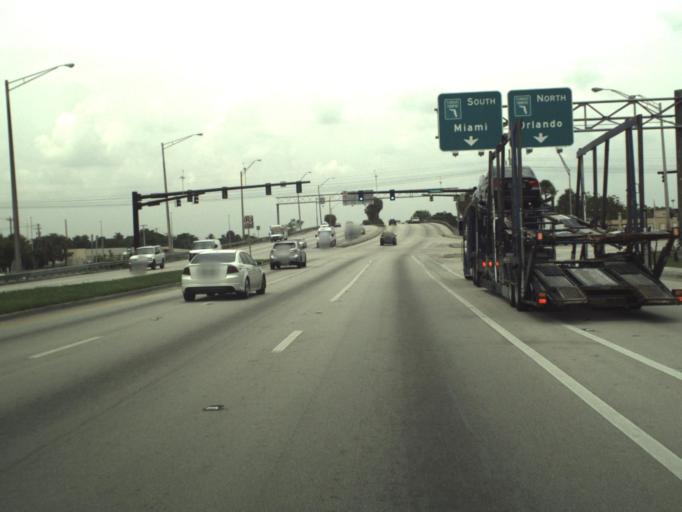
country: US
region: Florida
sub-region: Broward County
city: Lauderhill
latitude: 26.1360
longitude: -80.2157
